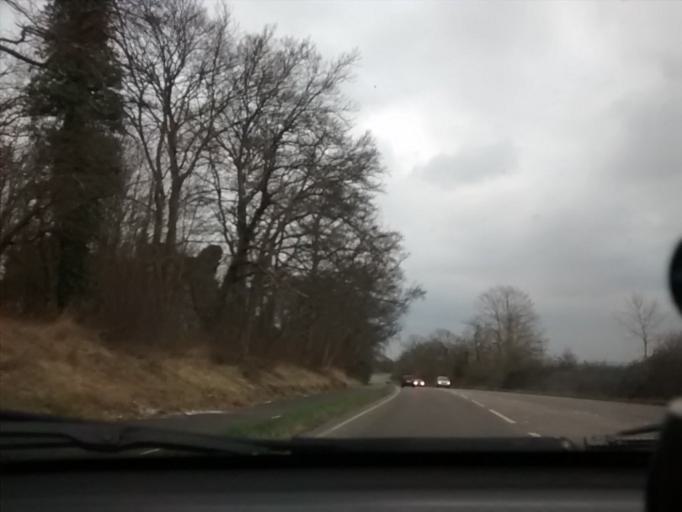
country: GB
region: England
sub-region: Cambridgeshire
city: Sawston
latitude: 52.1537
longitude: 0.1862
